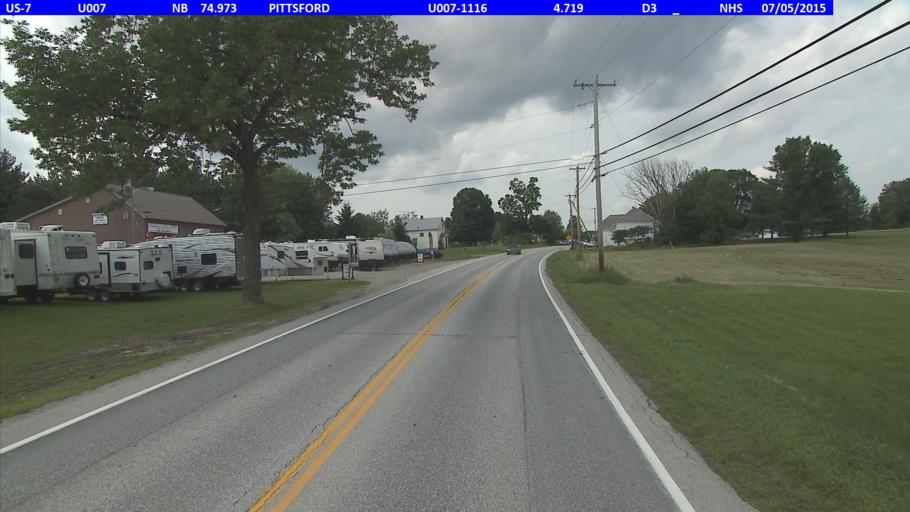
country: US
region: Vermont
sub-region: Rutland County
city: Brandon
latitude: 43.7157
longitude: -73.0389
